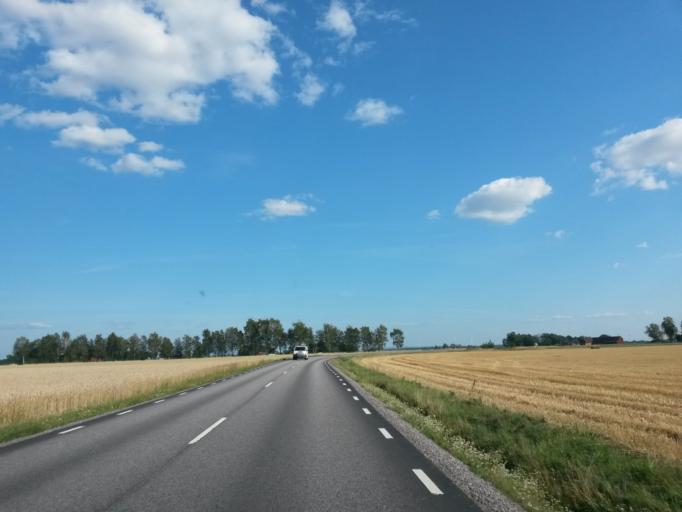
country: SE
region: Vaestra Goetaland
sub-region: Lidkopings Kommun
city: Lidkoping
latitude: 58.4187
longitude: 13.1621
